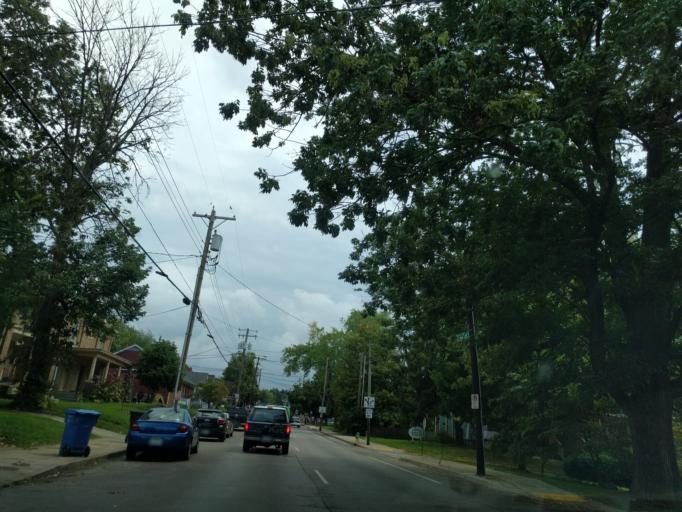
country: US
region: Kentucky
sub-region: Fayette County
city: Mount Vernon
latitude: 38.0376
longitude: -84.4947
